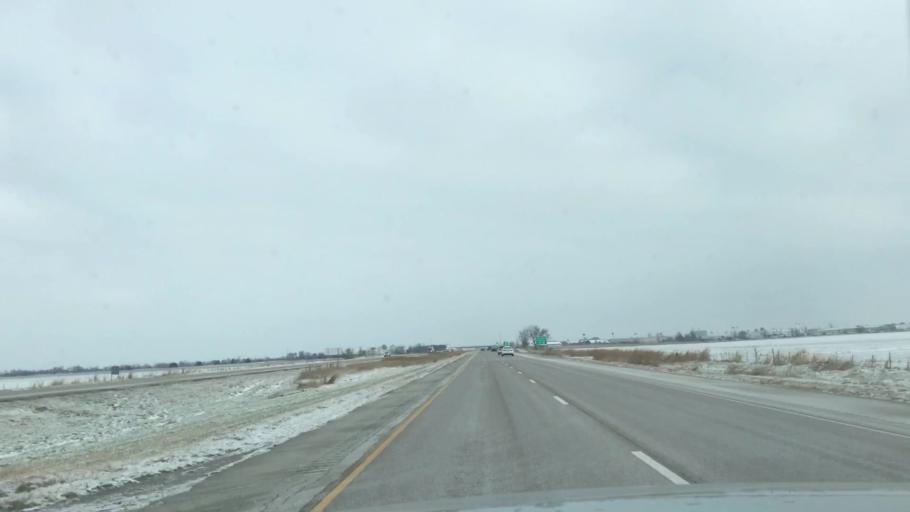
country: US
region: Illinois
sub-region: Montgomery County
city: Litchfield
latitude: 39.1602
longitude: -89.6909
